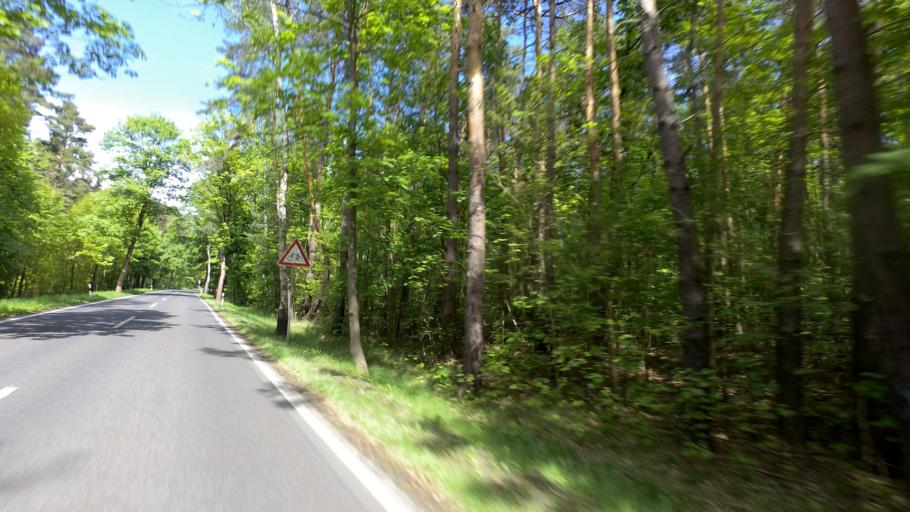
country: DE
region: Brandenburg
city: Sperenberg
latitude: 52.1615
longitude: 13.3662
